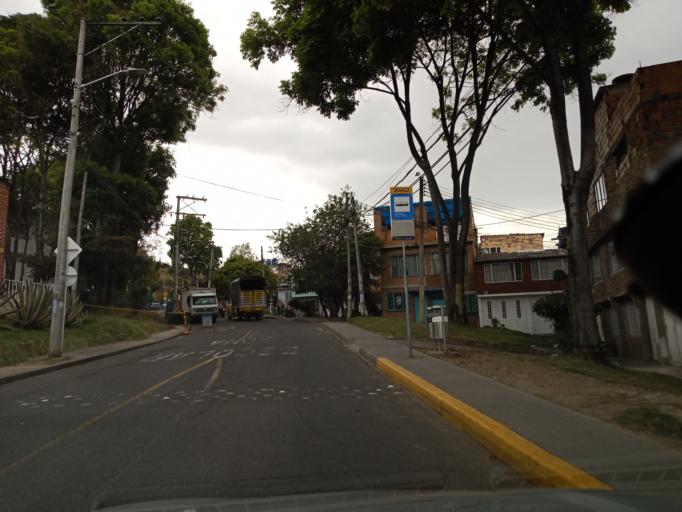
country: CO
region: Bogota D.C.
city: Bogota
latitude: 4.5667
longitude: -74.1039
